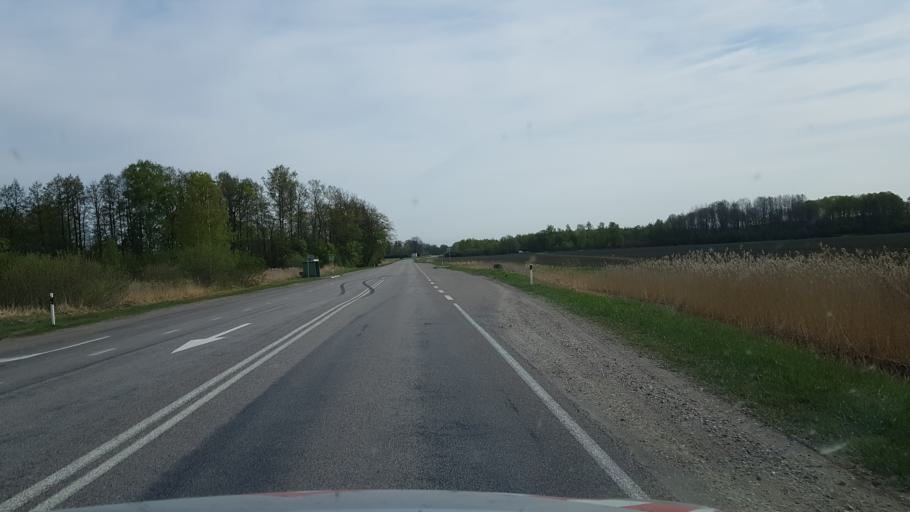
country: EE
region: Paernumaa
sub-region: Audru vald
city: Audru
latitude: 58.3930
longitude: 24.2804
